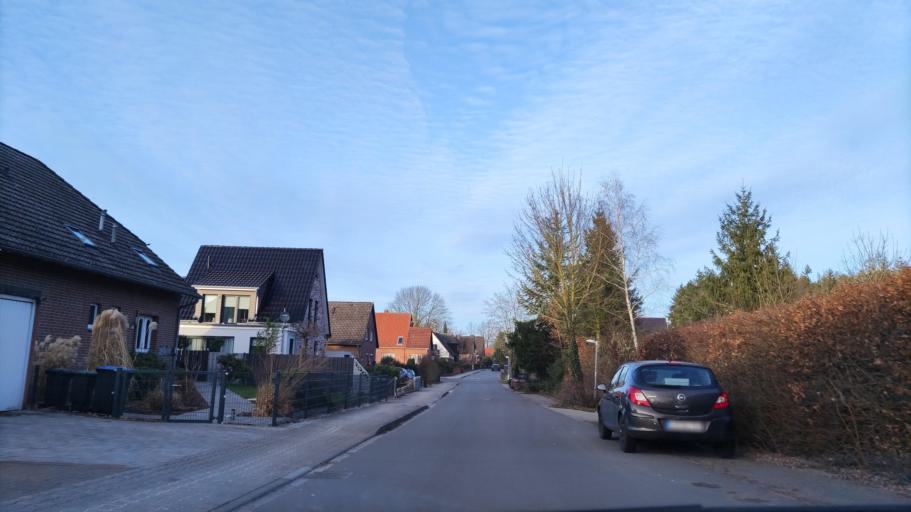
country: DE
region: Lower Saxony
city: Reppenstedt
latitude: 53.2488
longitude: 10.3682
